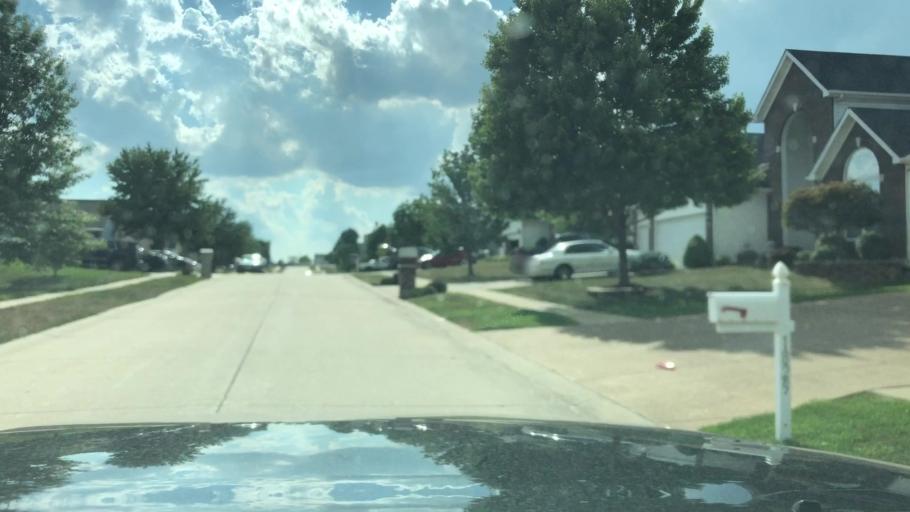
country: US
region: Missouri
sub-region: Saint Charles County
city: Wentzville
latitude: 38.8374
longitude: -90.8872
